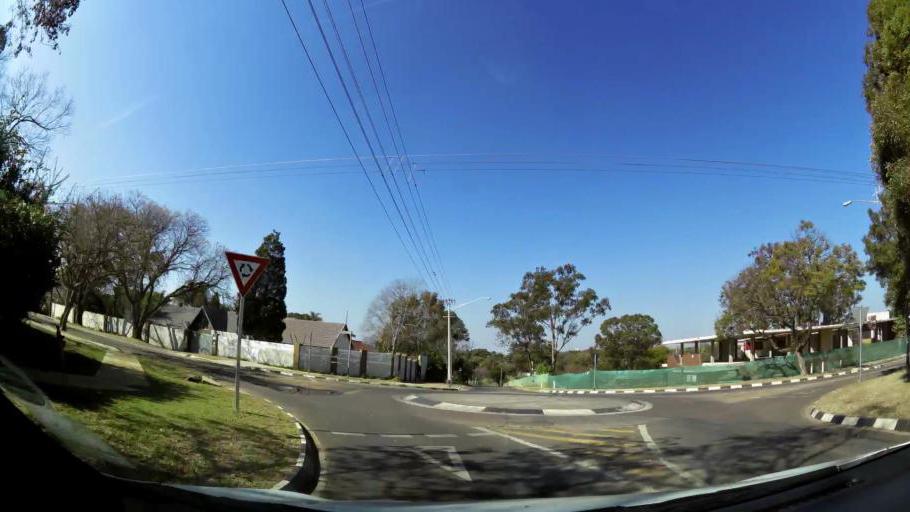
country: ZA
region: Gauteng
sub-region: City of Tshwane Metropolitan Municipality
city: Pretoria
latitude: -25.7789
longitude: 28.2600
